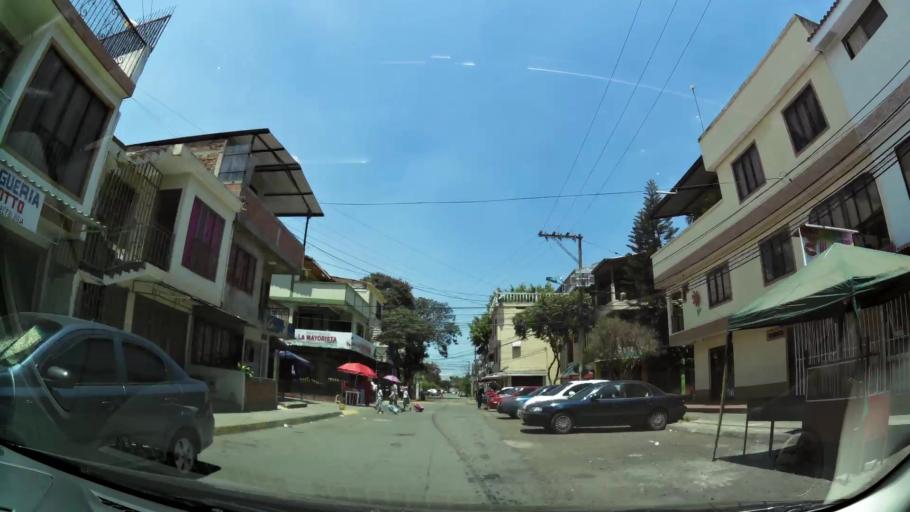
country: CO
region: Valle del Cauca
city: Cali
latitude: 3.4477
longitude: -76.4908
